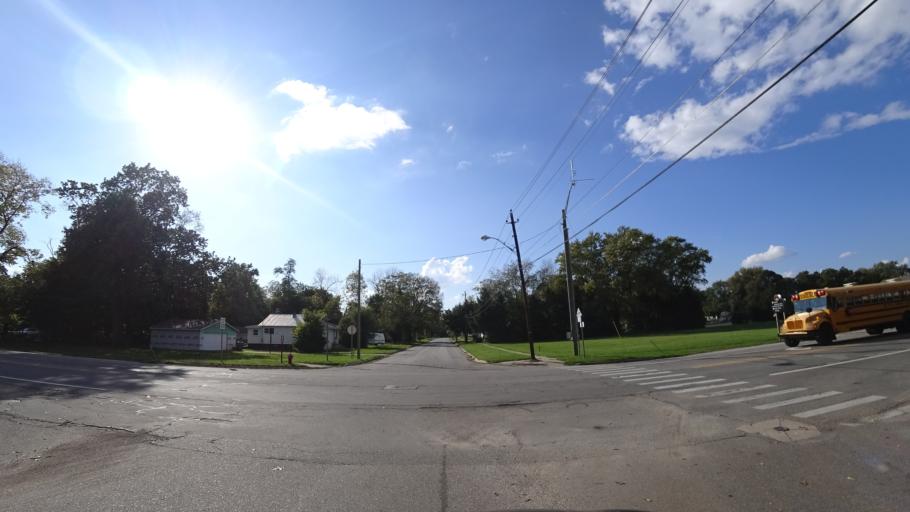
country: US
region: Michigan
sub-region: Saint Joseph County
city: Three Rivers
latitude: 41.9475
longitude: -85.6199
